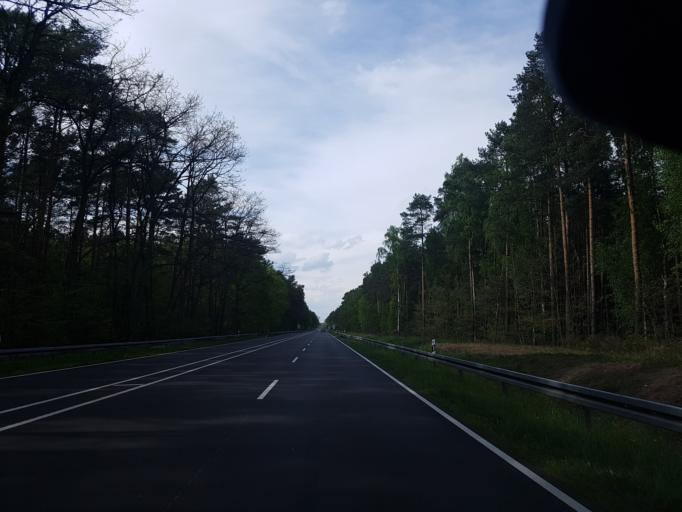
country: DE
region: Saxony
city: Gross Duben
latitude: 51.6539
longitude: 14.5347
